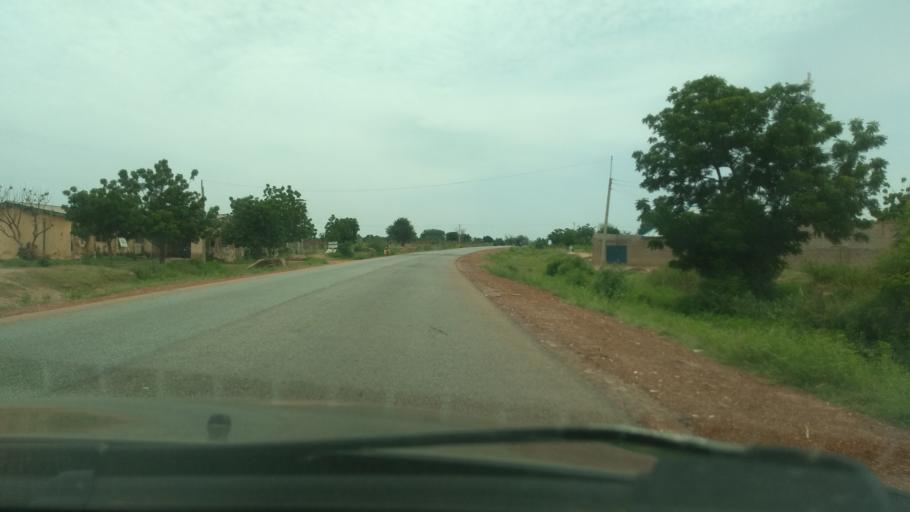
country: NG
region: Katsina
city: Kankia
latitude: 12.4071
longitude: 7.7210
